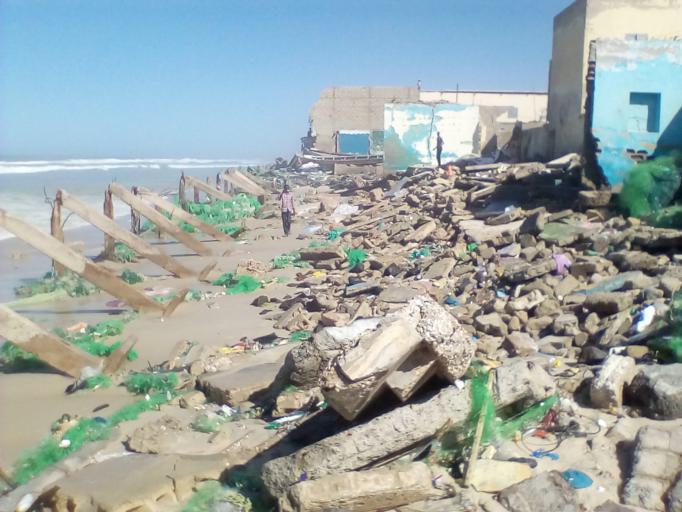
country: SN
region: Saint-Louis
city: Saint-Louis
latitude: 16.0190
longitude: -16.5095
